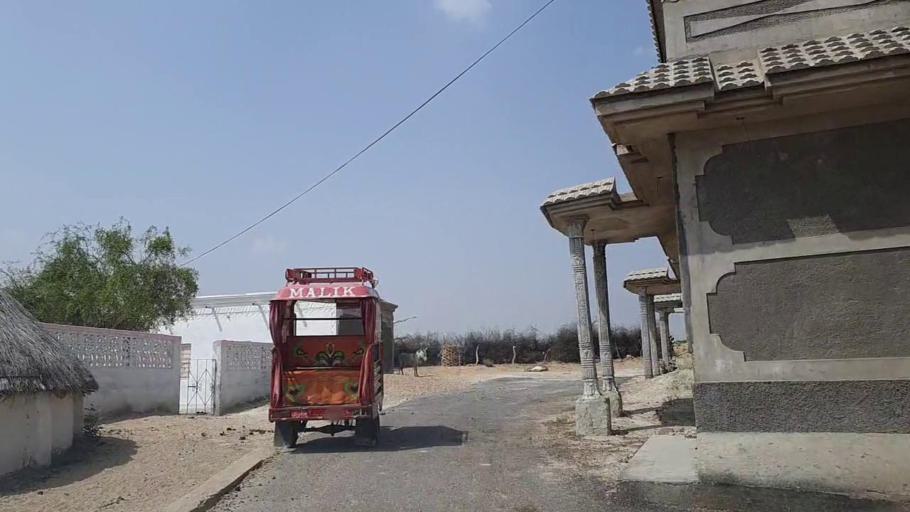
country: PK
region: Sindh
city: Mithi
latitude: 24.7854
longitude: 69.8784
